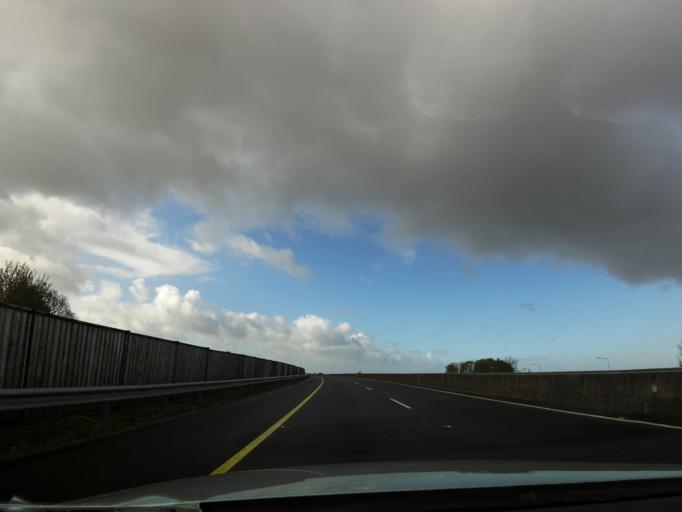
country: IE
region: Munster
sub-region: County Limerick
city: Annacotty
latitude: 52.6766
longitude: -8.5137
